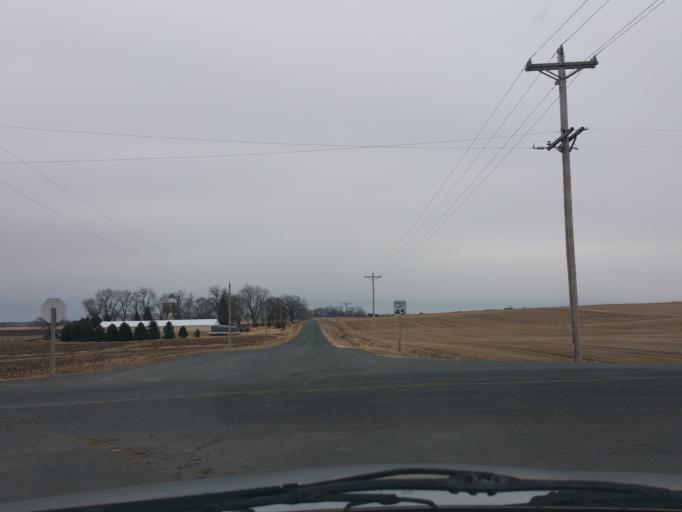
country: US
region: Wisconsin
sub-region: Saint Croix County
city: Roberts
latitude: 45.0071
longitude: -92.5582
